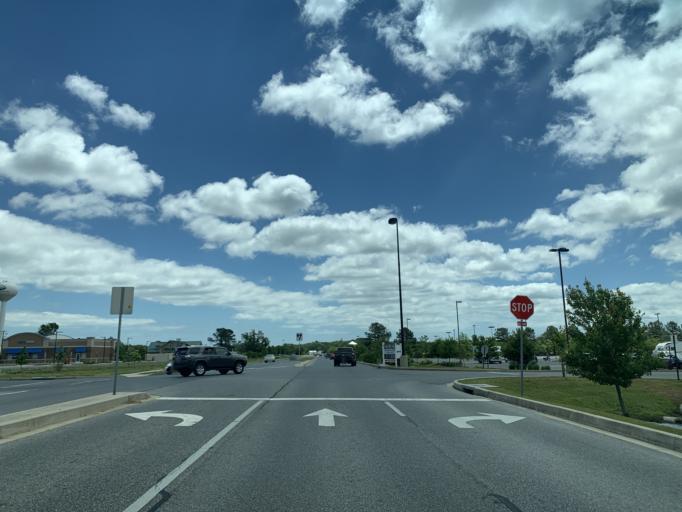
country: US
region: Maryland
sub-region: Worcester County
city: Ocean Pines
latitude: 38.3442
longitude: -75.1660
